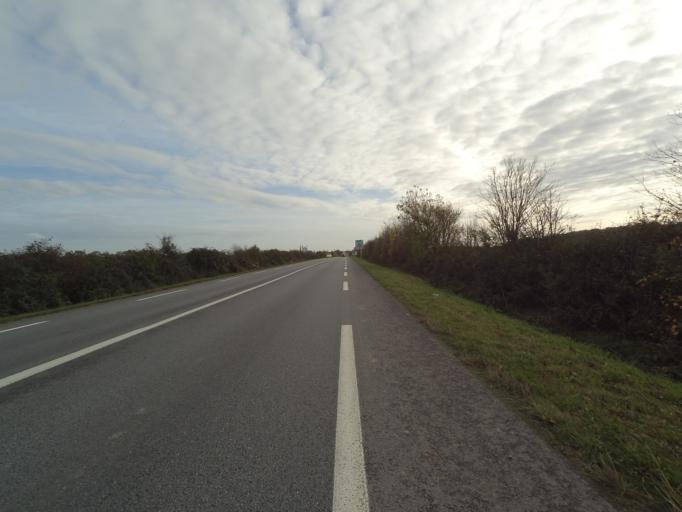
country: FR
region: Pays de la Loire
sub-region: Departement de la Vendee
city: Saint-Hilaire-de-Loulay
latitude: 47.0206
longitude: -1.3454
